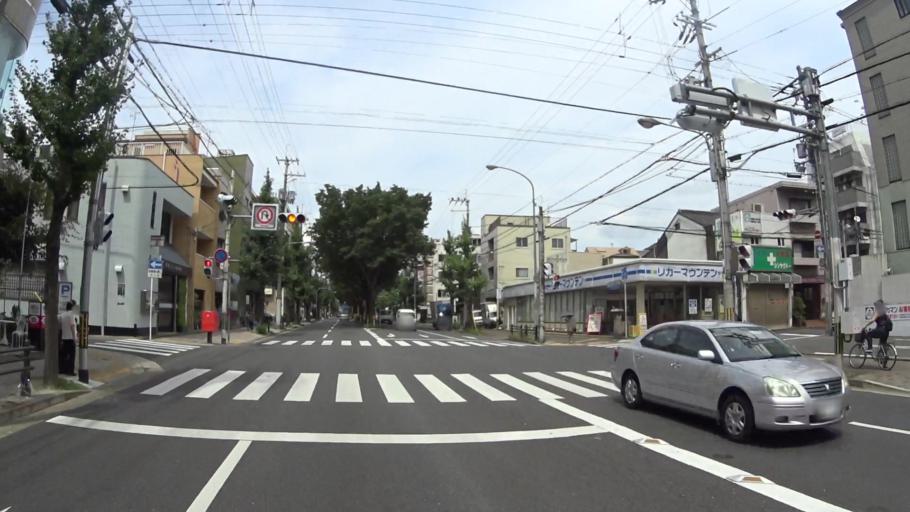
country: JP
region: Kyoto
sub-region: Kyoto-shi
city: Kamigyo-ku
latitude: 35.0293
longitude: 135.7914
